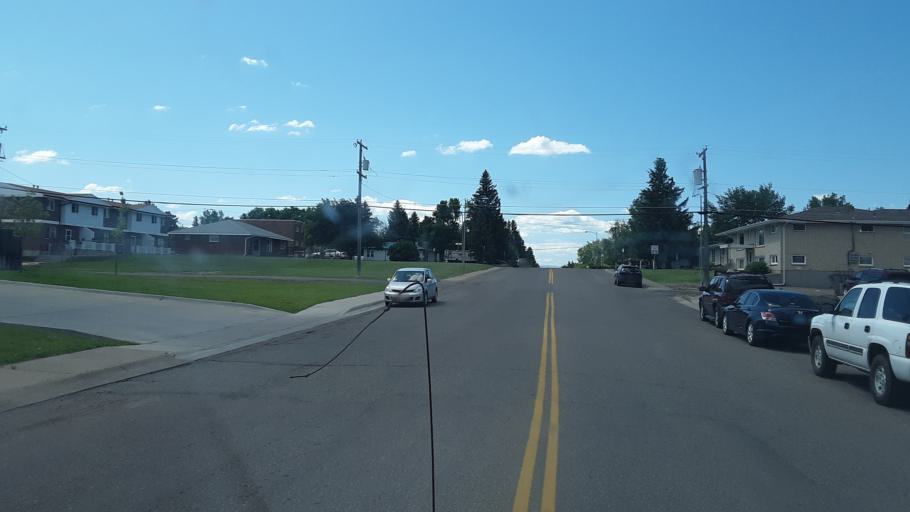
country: US
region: Montana
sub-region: Cascade County
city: Great Falls
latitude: 47.4938
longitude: -111.2500
